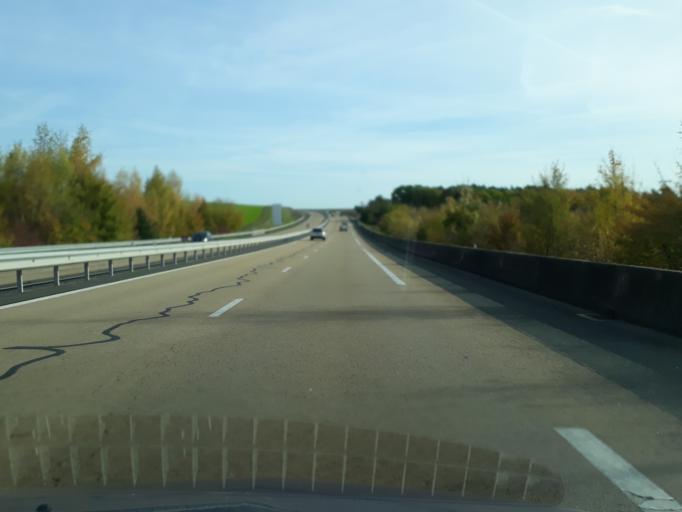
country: FR
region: Champagne-Ardenne
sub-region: Departement de l'Aube
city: Aix-en-Othe
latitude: 48.2578
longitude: 3.6550
